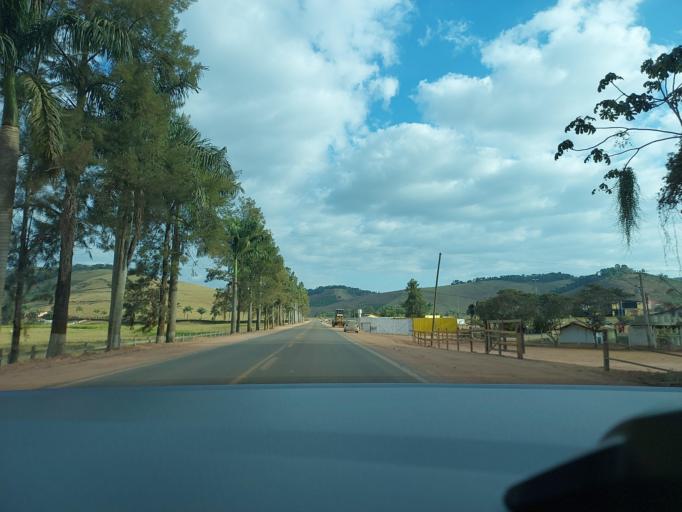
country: BR
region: Minas Gerais
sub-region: Visconde Do Rio Branco
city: Visconde do Rio Branco
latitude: -20.8590
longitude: -42.6683
